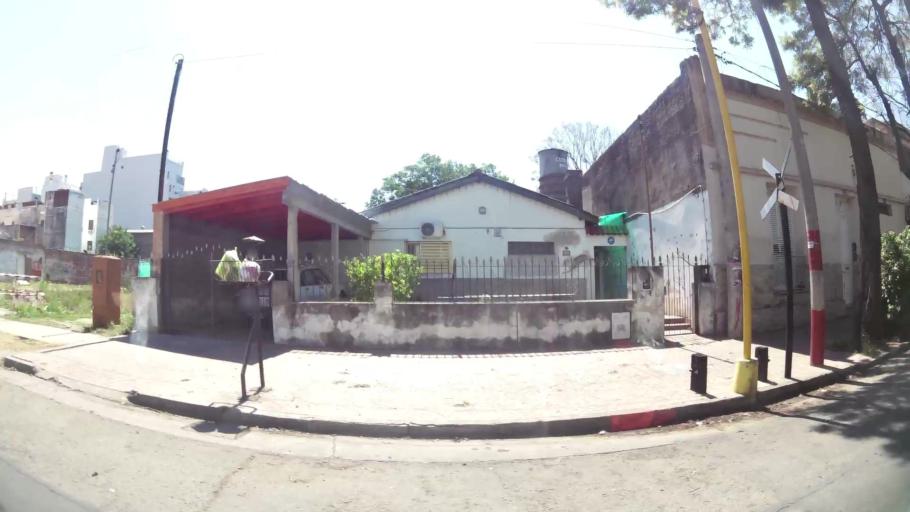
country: AR
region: Cordoba
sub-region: Departamento de Capital
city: Cordoba
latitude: -31.3961
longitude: -64.1860
